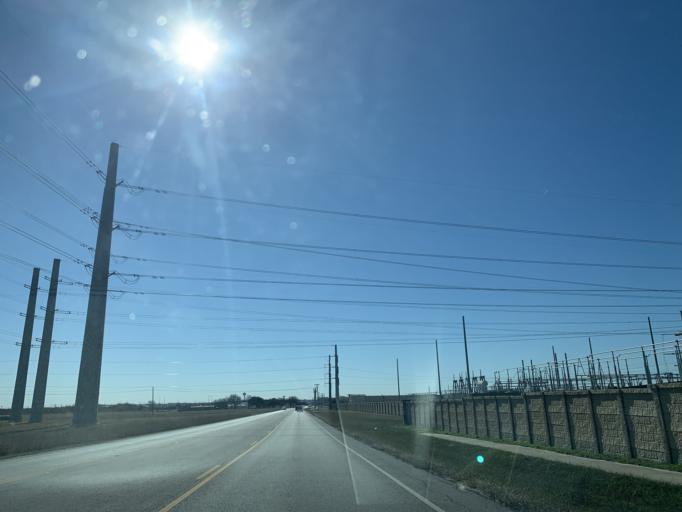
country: US
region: Texas
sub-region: Williamson County
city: Hutto
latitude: 30.5529
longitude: -97.5598
